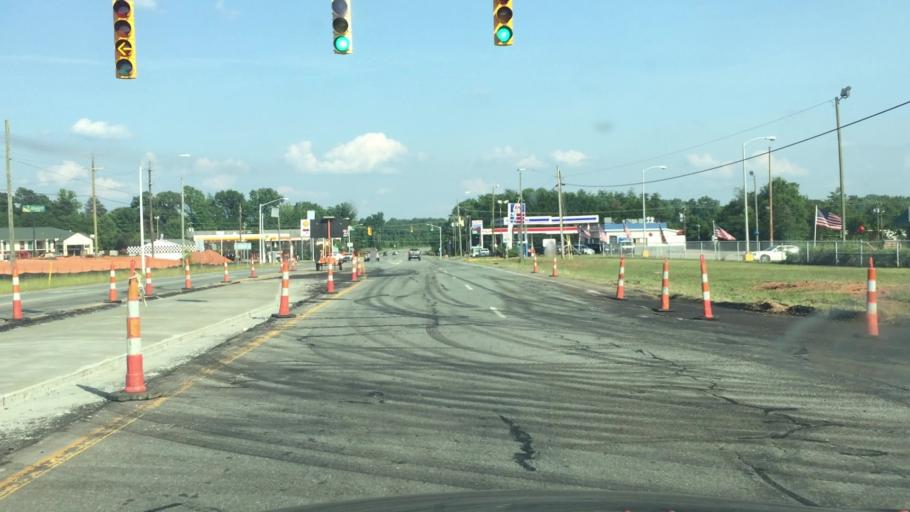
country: US
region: North Carolina
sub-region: Rockingham County
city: Reidsville
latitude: 36.3264
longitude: -79.6420
